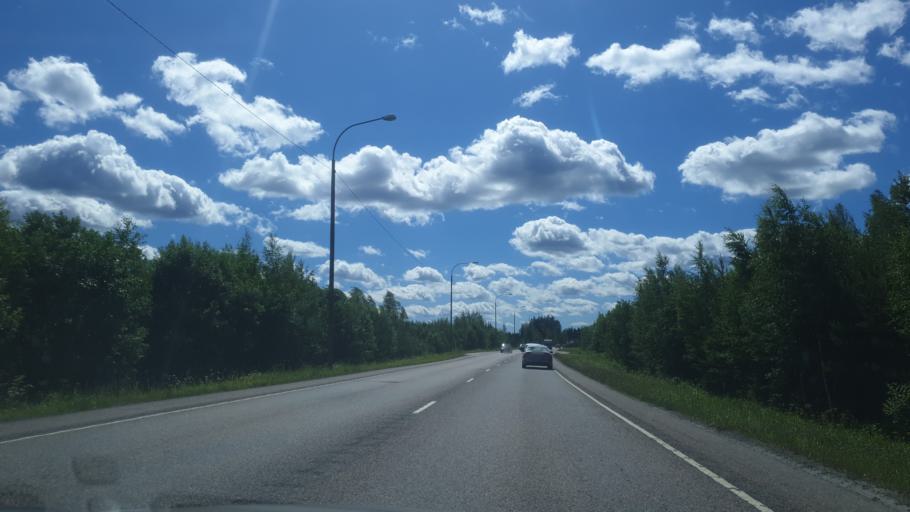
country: FI
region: Northern Savo
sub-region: Varkaus
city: Leppaevirta
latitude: 62.4066
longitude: 27.8260
